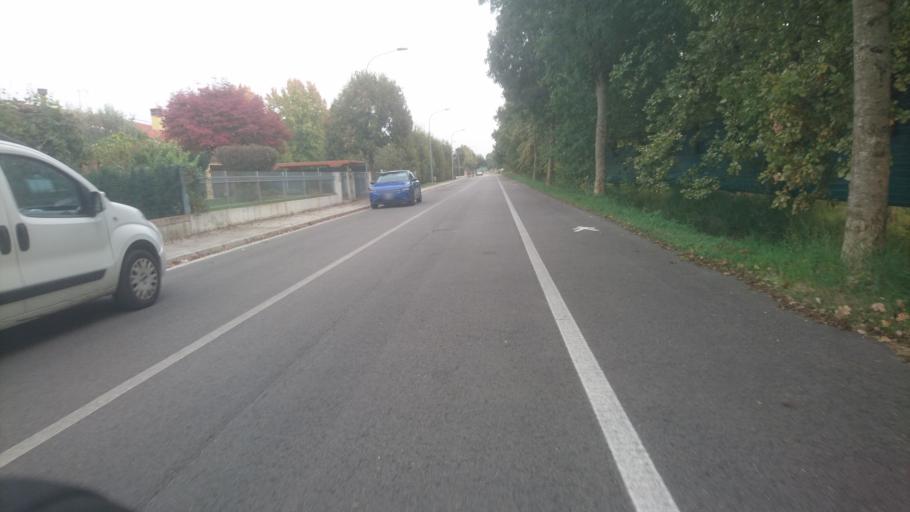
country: IT
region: Veneto
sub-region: Provincia di Vicenza
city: Montegalda
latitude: 45.4475
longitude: 11.6825
